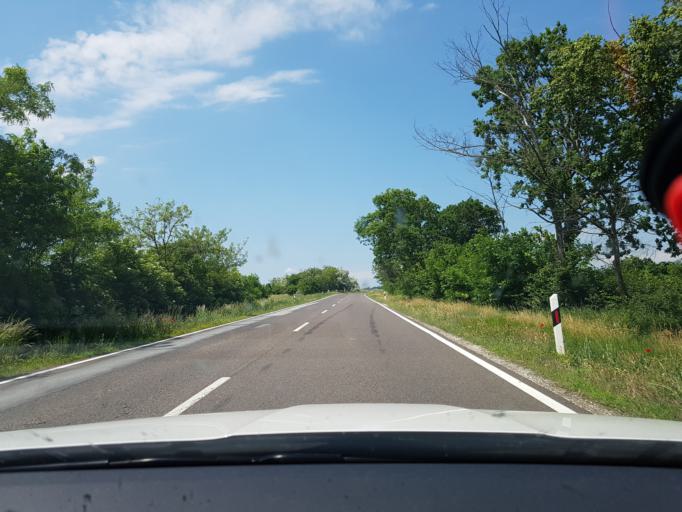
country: HU
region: Hajdu-Bihar
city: Egyek
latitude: 47.5506
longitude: 20.8824
